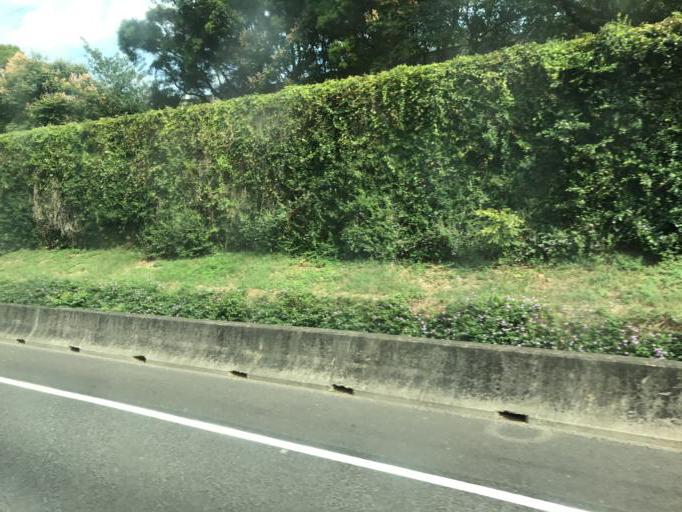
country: TW
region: Taiwan
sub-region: Hsinchu
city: Hsinchu
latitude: 24.7732
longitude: 121.0037
